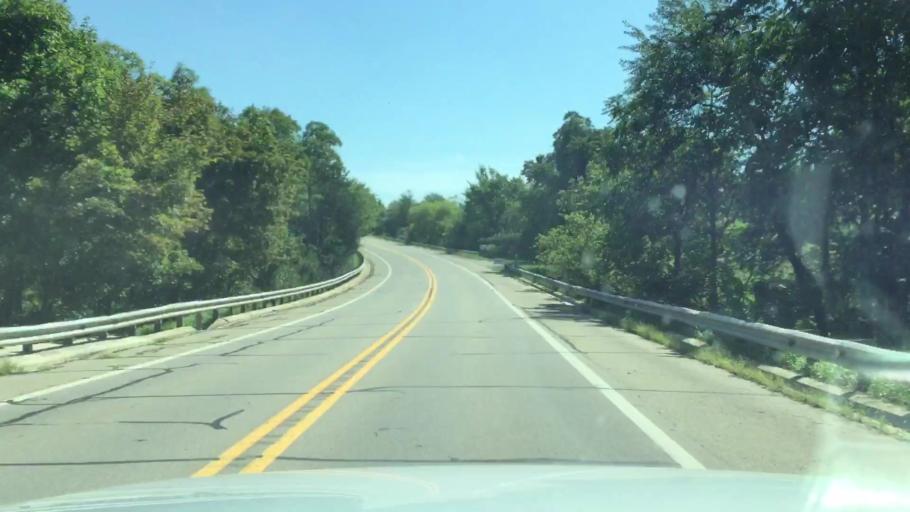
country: US
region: Michigan
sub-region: Jackson County
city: Brooklyn
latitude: 42.0584
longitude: -84.1767
